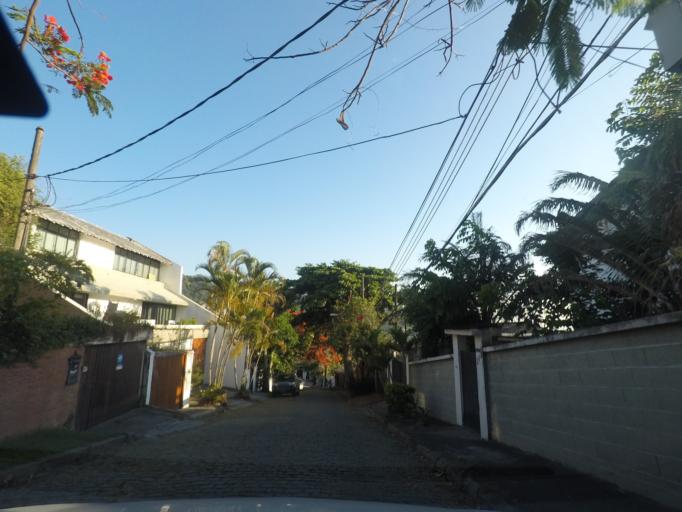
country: BR
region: Rio de Janeiro
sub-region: Rio De Janeiro
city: Rio de Janeiro
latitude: -22.9418
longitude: -43.1943
